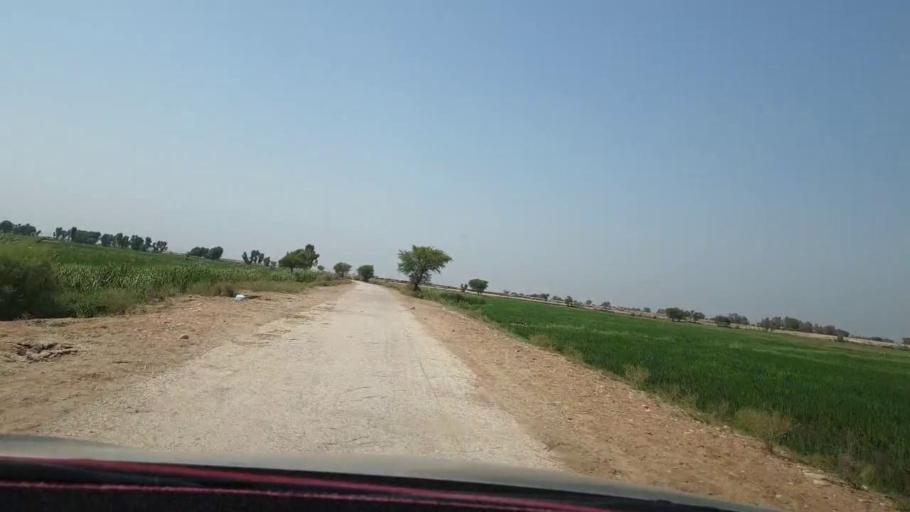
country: PK
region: Sindh
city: Warah
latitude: 27.5480
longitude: 67.7407
